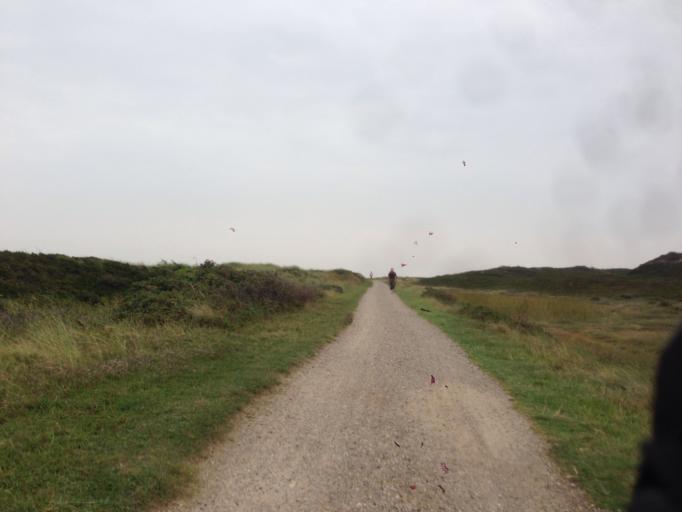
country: DE
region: Schleswig-Holstein
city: Westerland
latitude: 54.8383
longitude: 8.2938
